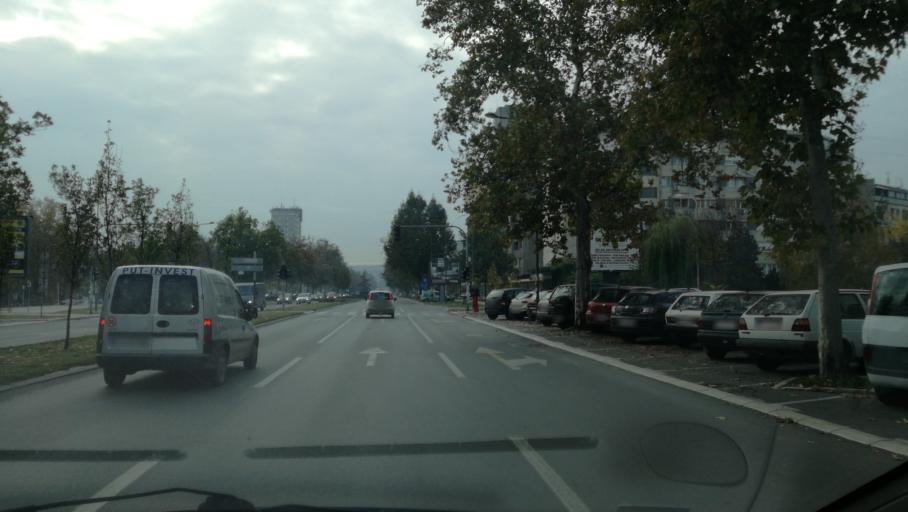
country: RS
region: Autonomna Pokrajina Vojvodina
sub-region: Juznobacki Okrug
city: Novi Sad
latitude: 45.2471
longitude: 19.8395
